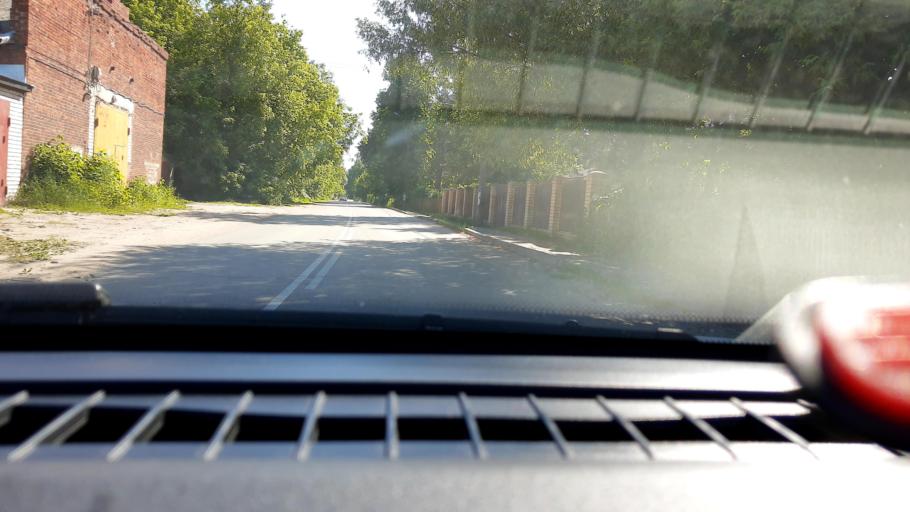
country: RU
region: Nizjnij Novgorod
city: Gidrotorf
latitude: 56.5253
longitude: 43.5492
